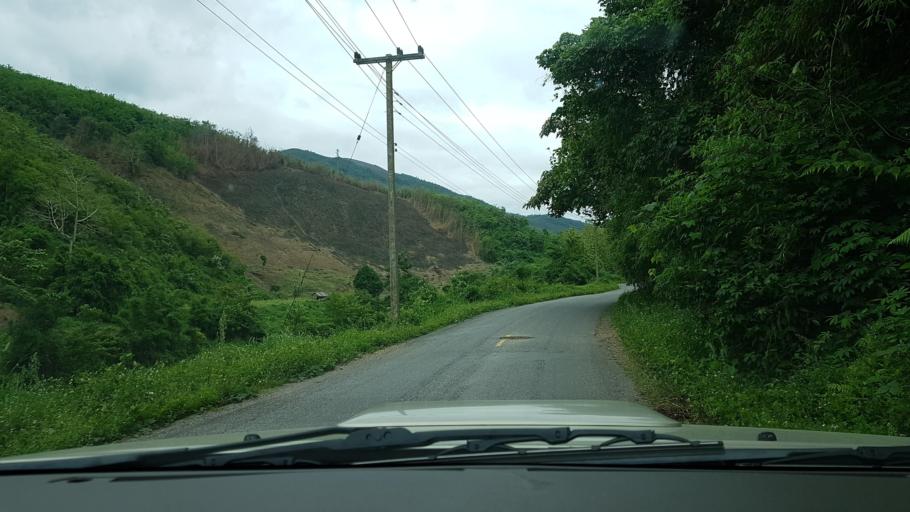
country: LA
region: Oudomxai
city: Muang La
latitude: 20.9746
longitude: 102.2237
